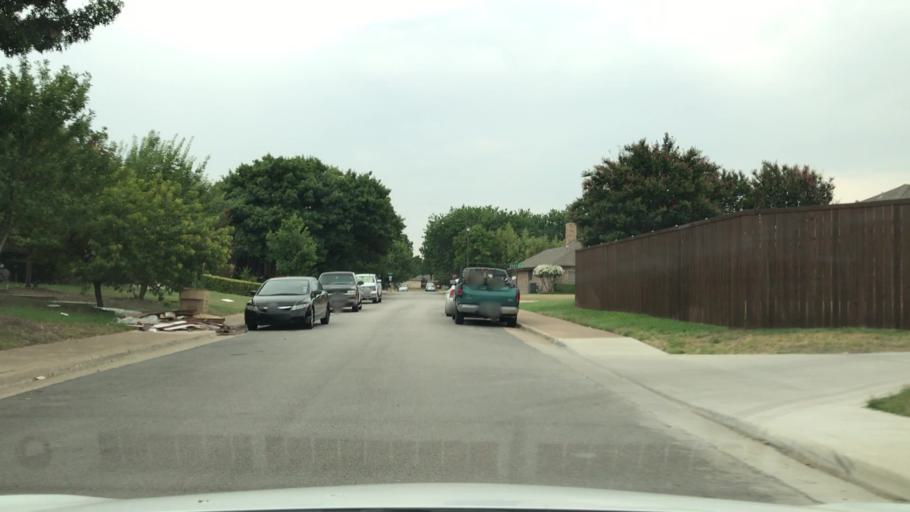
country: US
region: Texas
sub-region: Dallas County
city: Carrollton
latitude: 32.9947
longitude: -96.8672
